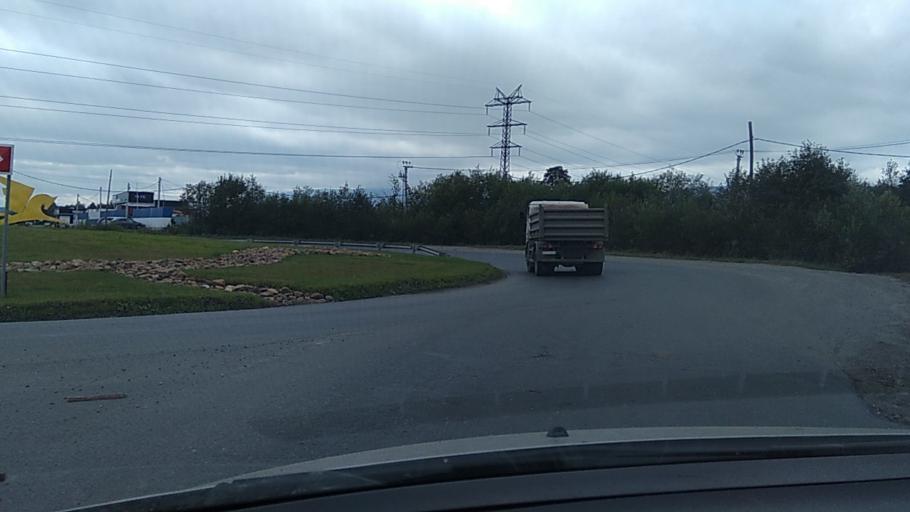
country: RU
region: Chelyabinsk
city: Zlatoust
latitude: 55.1174
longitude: 59.6976
